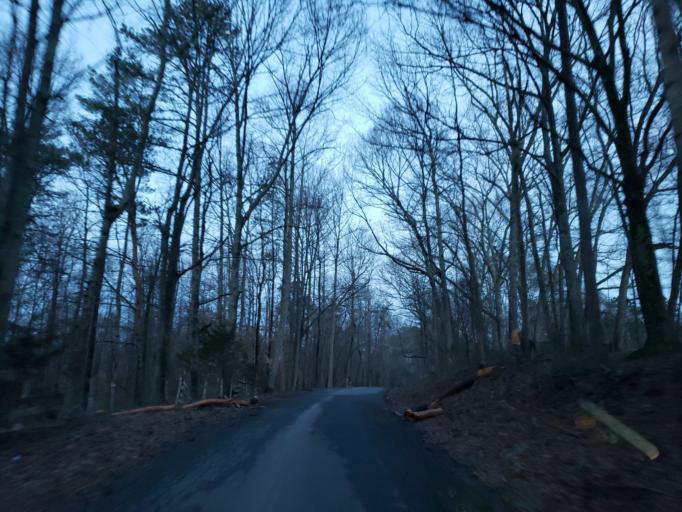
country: US
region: Georgia
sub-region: Cherokee County
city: Ball Ground
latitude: 34.2917
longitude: -84.2902
